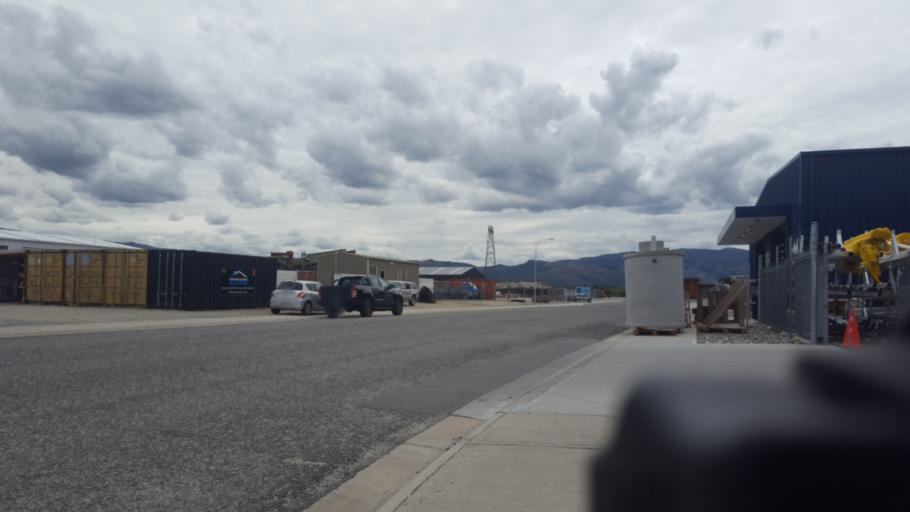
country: NZ
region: Otago
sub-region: Queenstown-Lakes District
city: Wanaka
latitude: -45.2475
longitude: 169.3712
